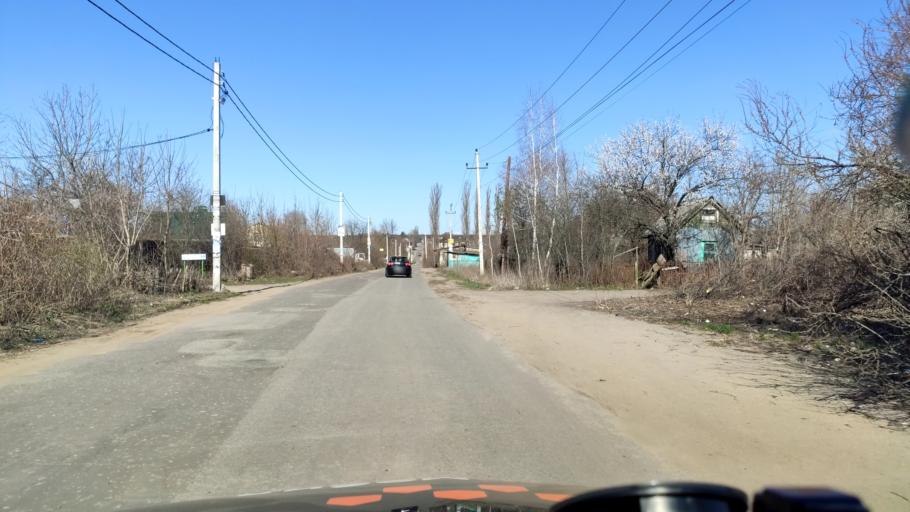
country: RU
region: Voronezj
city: Shilovo
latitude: 51.5936
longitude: 39.1554
